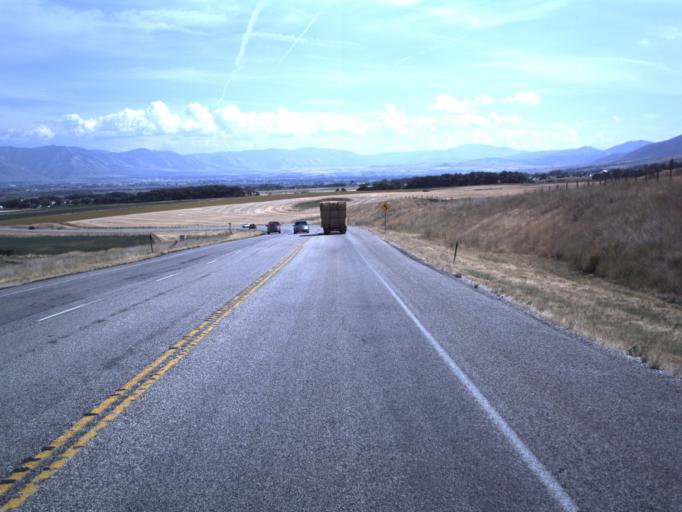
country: US
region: Utah
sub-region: Cache County
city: Mendon
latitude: 41.7591
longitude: -112.0056
